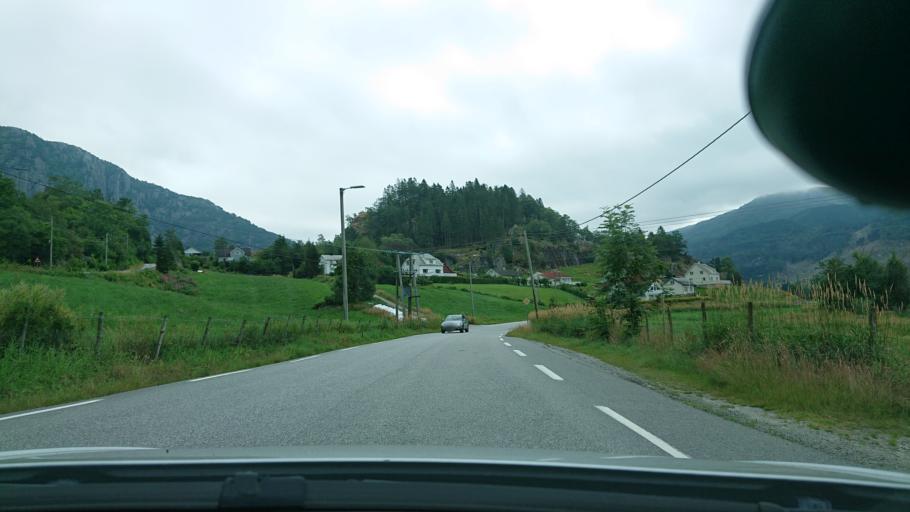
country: NO
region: Rogaland
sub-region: Hjelmeland
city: Hjelmelandsvagen
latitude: 59.2342
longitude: 6.1879
